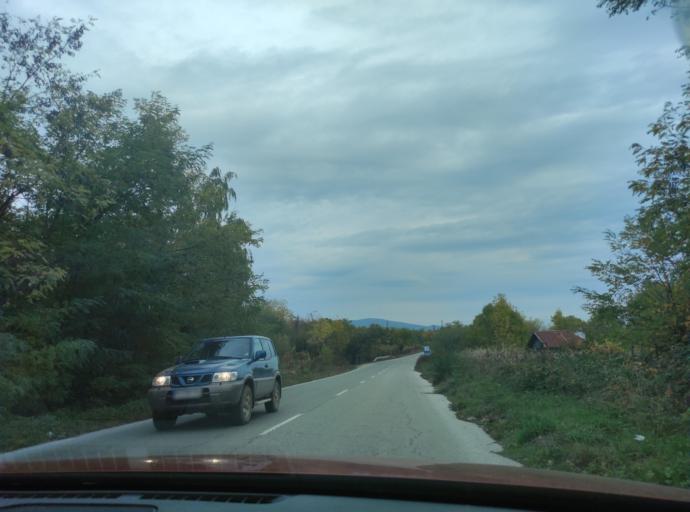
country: BG
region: Montana
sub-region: Obshtina Berkovitsa
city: Berkovitsa
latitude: 43.2097
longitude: 23.1595
